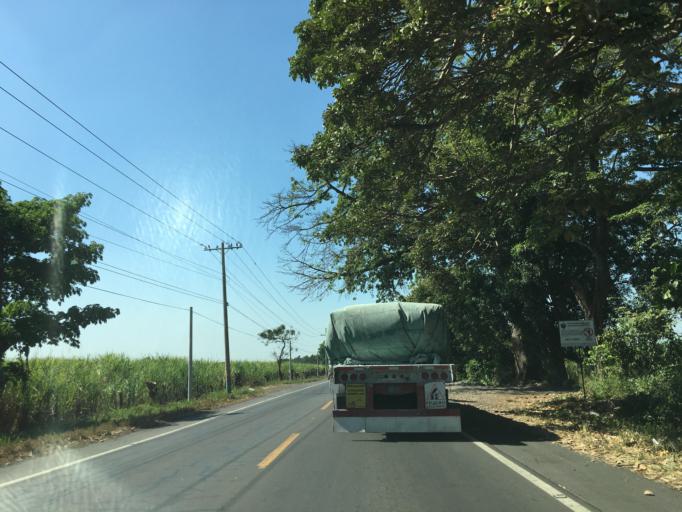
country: GT
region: Escuintla
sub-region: Municipio de Masagua
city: Masagua
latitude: 14.1937
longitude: -90.8553
